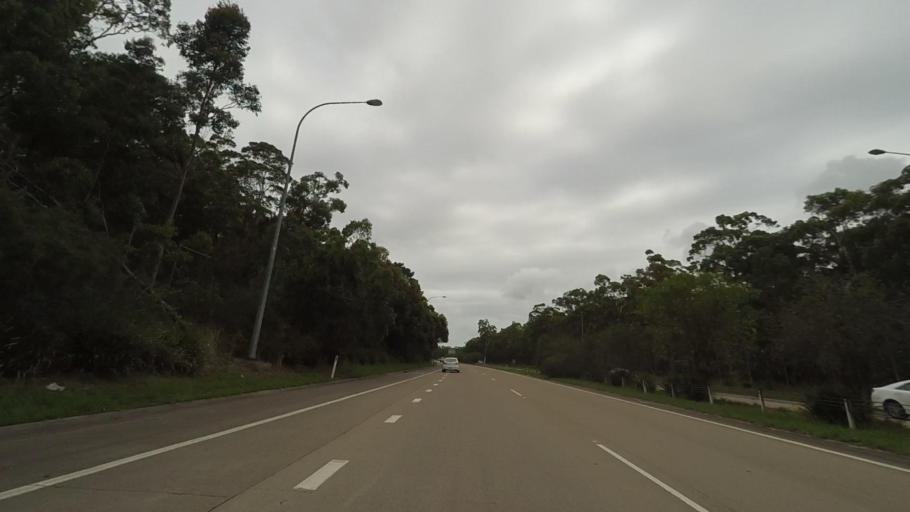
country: AU
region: New South Wales
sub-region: Lake Macquarie Shire
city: Cardiff South
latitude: -32.9633
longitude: 151.6765
